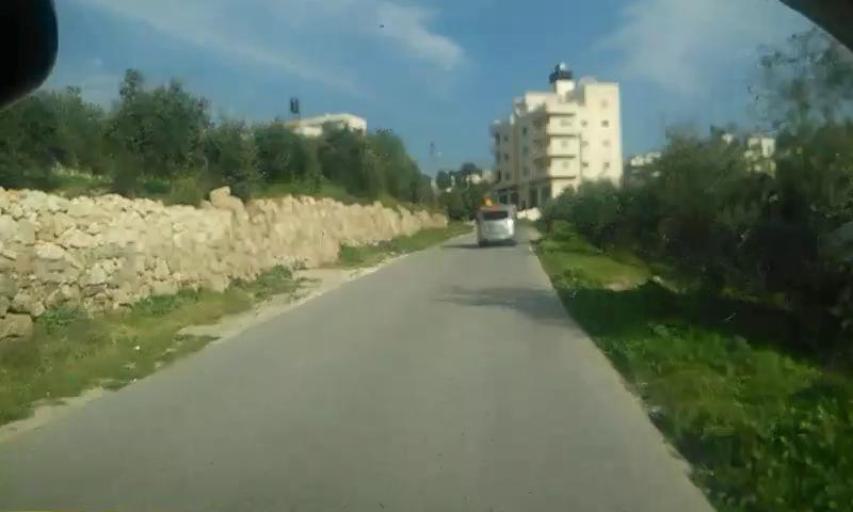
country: PS
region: West Bank
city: Nuba
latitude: 31.6142
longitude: 35.0234
